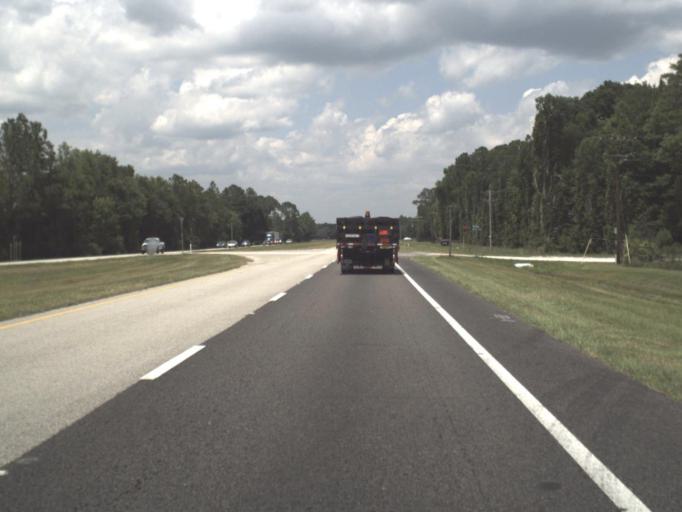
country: US
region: Florida
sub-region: Alachua County
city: Waldo
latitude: 29.7756
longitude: -82.1868
